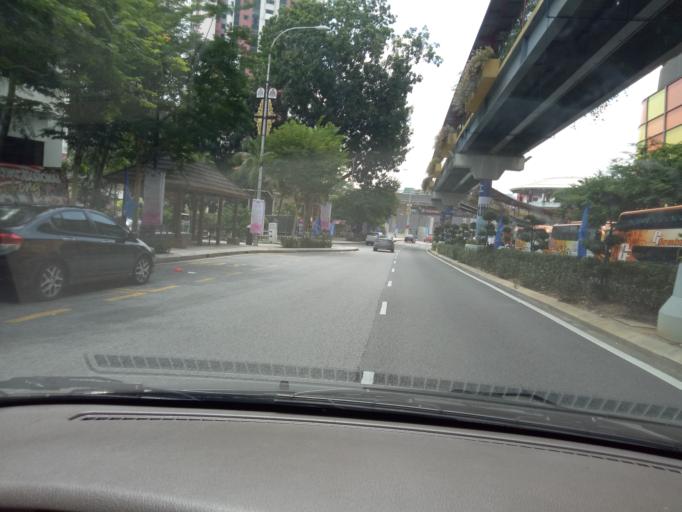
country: MY
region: Kuala Lumpur
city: Kuala Lumpur
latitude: 3.1666
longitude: 101.6915
